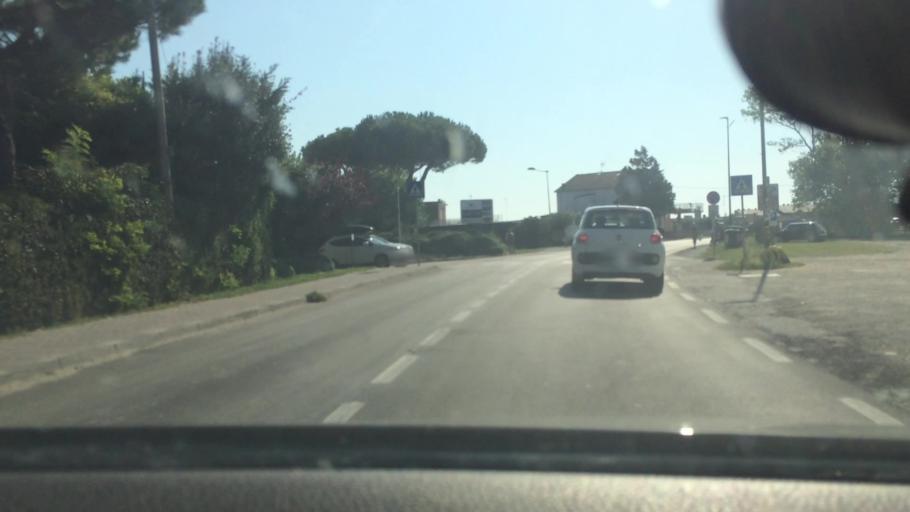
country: IT
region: Emilia-Romagna
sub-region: Provincia di Ferrara
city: Porto Garibaldi
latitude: 44.6888
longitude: 12.2376
